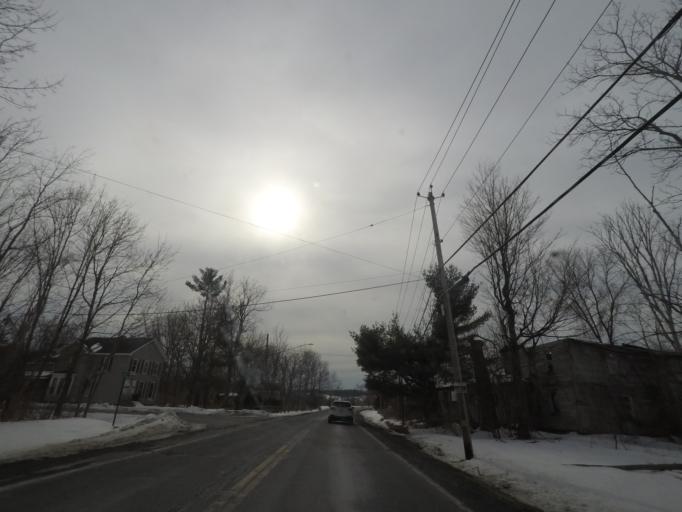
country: US
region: New York
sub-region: Albany County
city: Altamont
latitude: 42.6677
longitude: -74.1213
